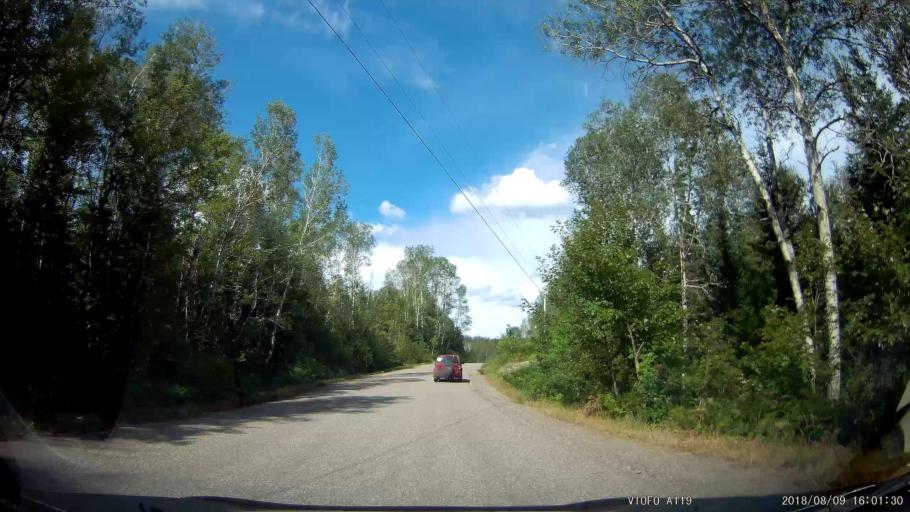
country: CA
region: Ontario
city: Rayside-Balfour
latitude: 46.6138
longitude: -81.4695
